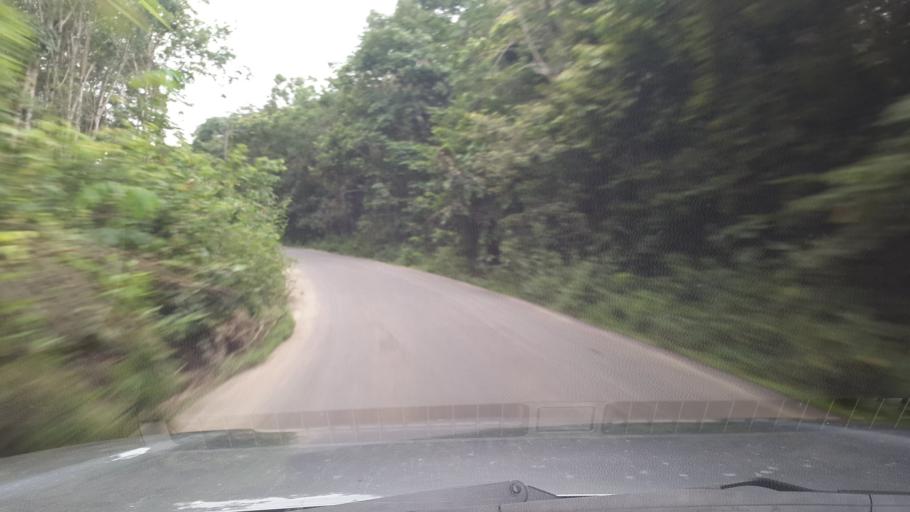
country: ID
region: South Sumatra
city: Gunungmenang
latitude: -3.1348
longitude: 103.9399
